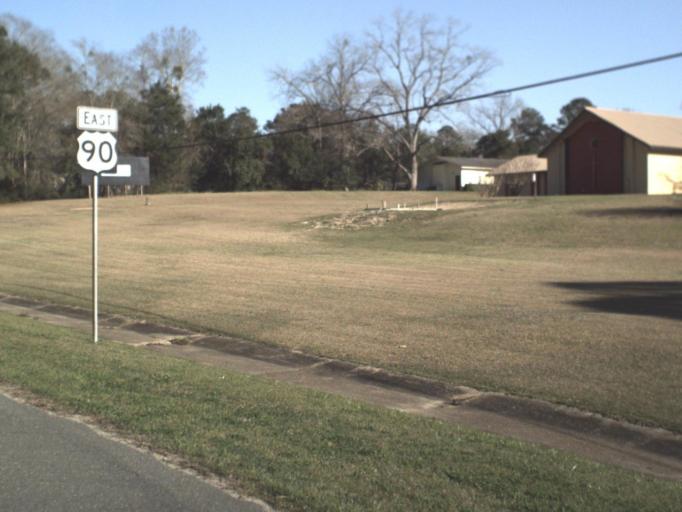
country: US
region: Florida
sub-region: Jackson County
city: Marianna
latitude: 30.7842
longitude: -85.2771
